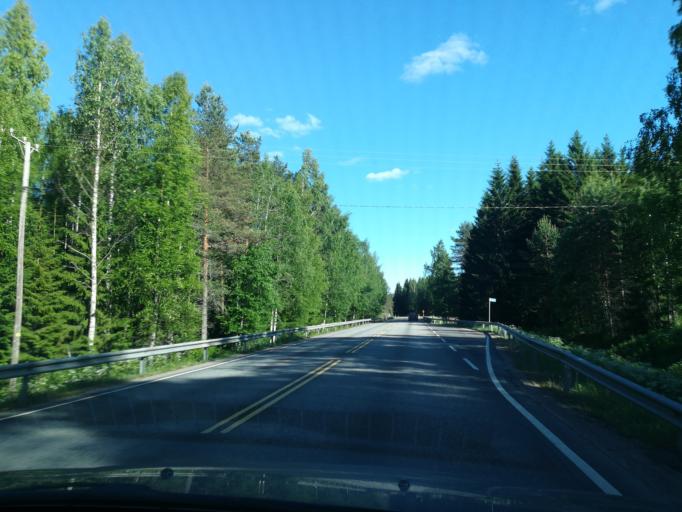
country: FI
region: South Karelia
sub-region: Imatra
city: Ruokolahti
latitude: 61.3685
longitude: 28.6782
